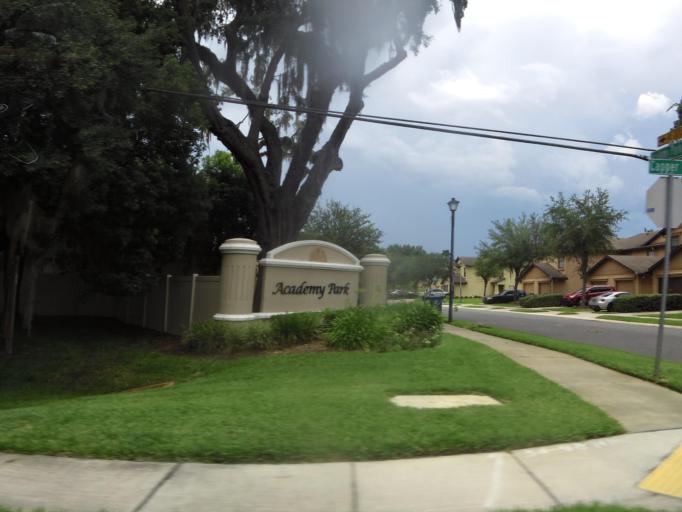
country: US
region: Florida
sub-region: Duval County
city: Jacksonville
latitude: 30.4278
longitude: -81.6991
